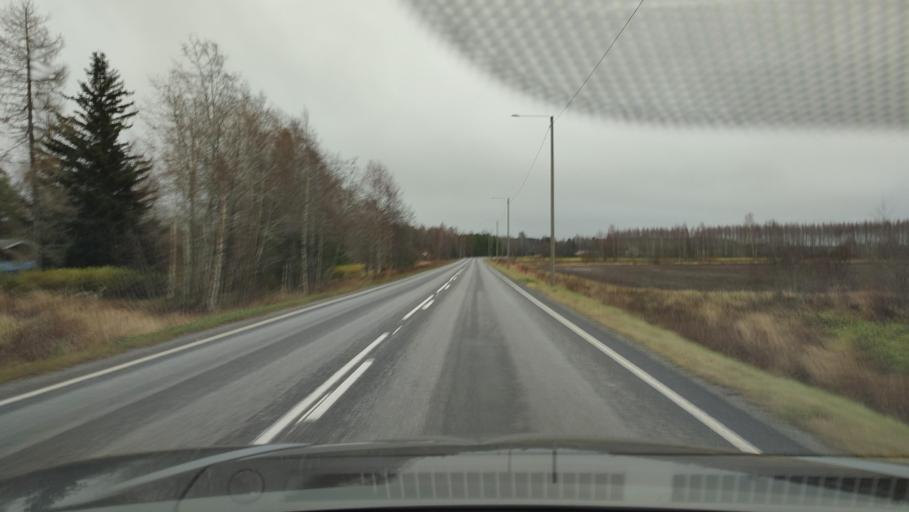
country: FI
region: Southern Ostrobothnia
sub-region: Suupohja
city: Isojoki
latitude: 62.1654
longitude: 21.8590
